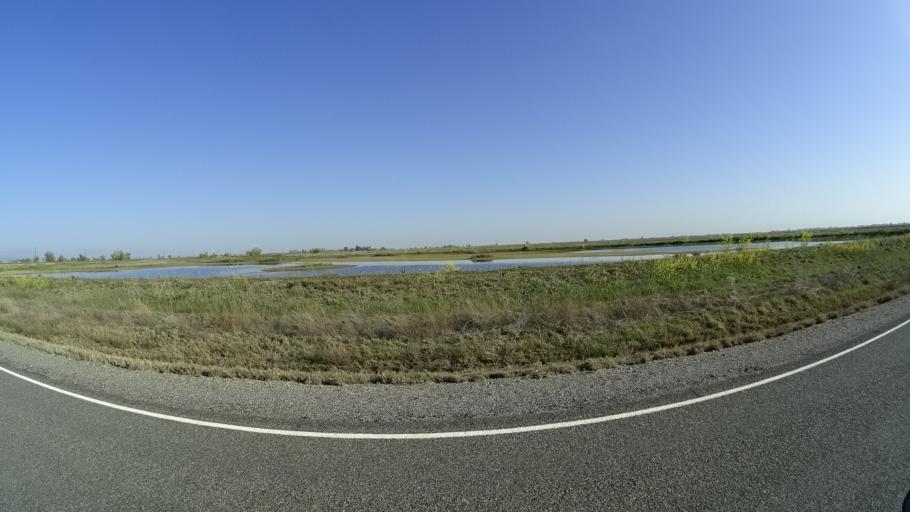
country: US
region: California
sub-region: Glenn County
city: Willows
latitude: 39.4071
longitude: -122.1790
